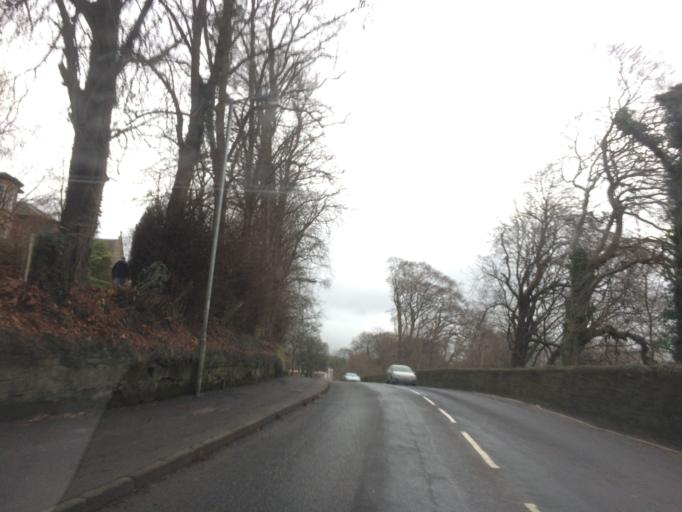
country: GB
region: Scotland
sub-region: East Renfrewshire
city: Giffnock
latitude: 55.8042
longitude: -4.3194
